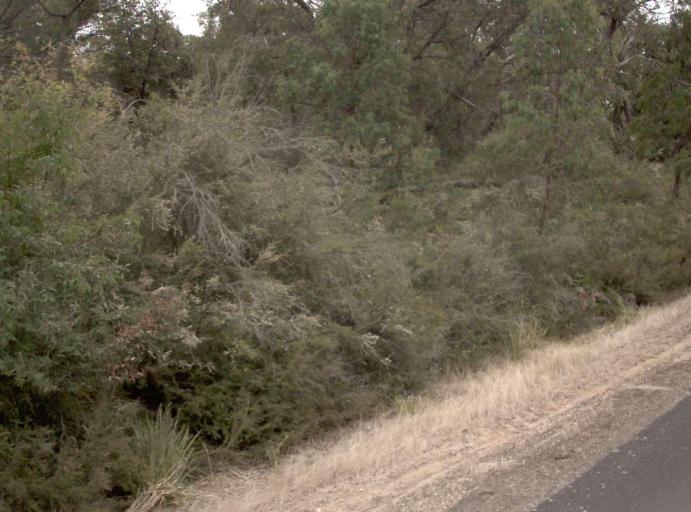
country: AU
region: Victoria
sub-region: Wellington
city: Sale
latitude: -38.2708
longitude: 147.0354
